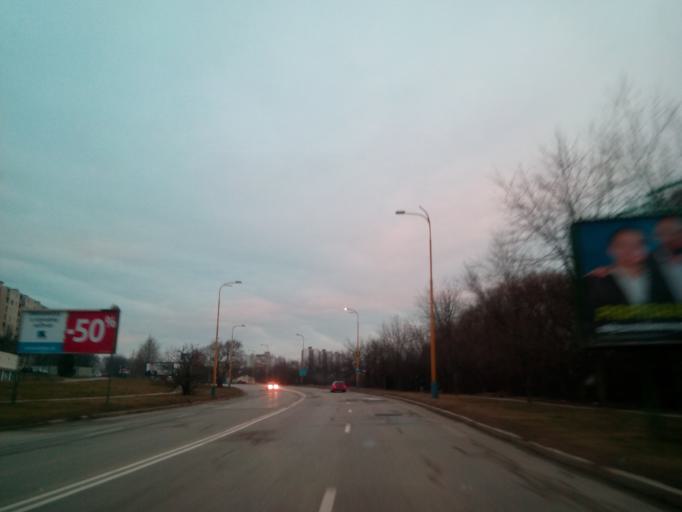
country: SK
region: Kosicky
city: Kosice
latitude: 48.7075
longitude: 21.2192
